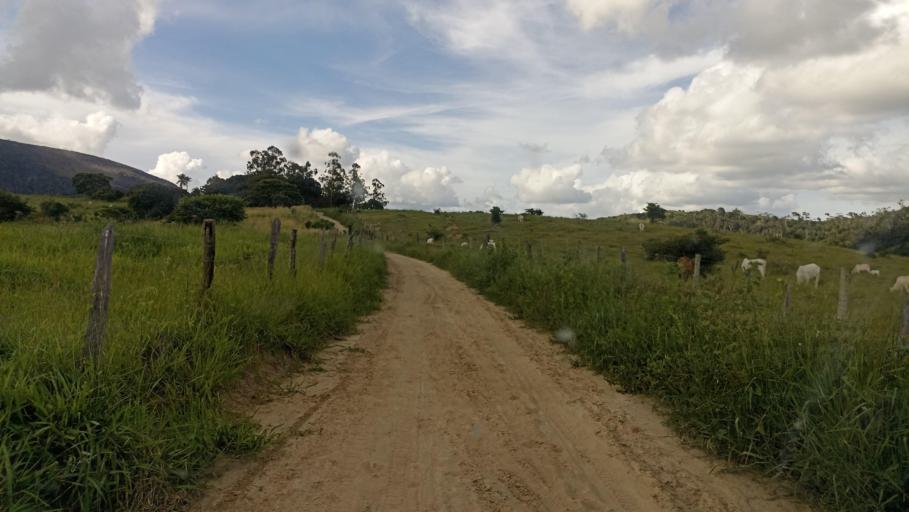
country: BR
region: Minas Gerais
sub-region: Almenara
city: Almenara
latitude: -16.6151
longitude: -40.4663
